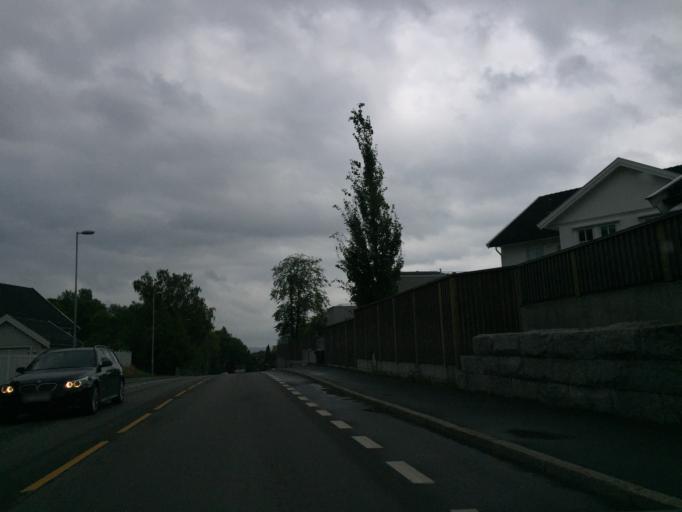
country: NO
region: Oslo
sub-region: Oslo
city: Sjolyststranda
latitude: 59.9460
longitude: 10.6780
